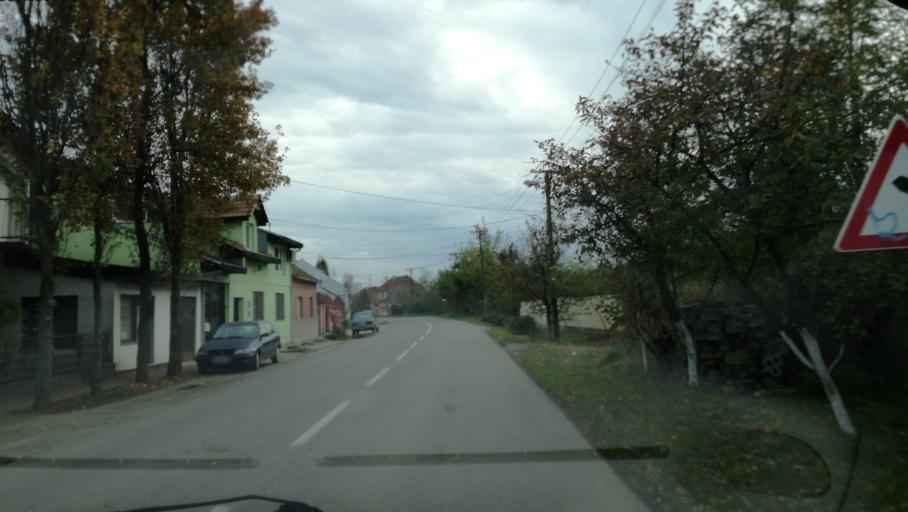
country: RS
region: Autonomna Pokrajina Vojvodina
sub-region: Severnobanatski Okrug
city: Kikinda
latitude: 45.8426
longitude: 20.4688
